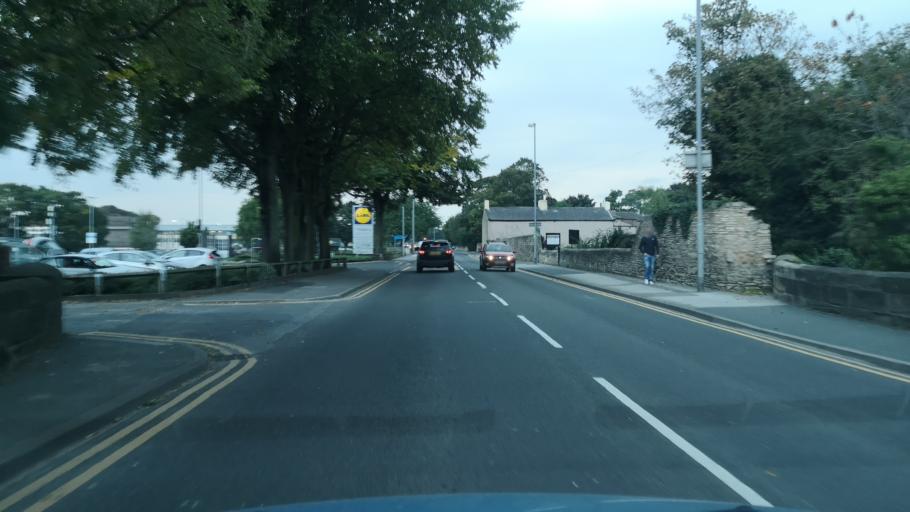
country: GB
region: England
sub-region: City and Borough of Wakefield
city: Knottingley
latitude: 53.7095
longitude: -1.2475
